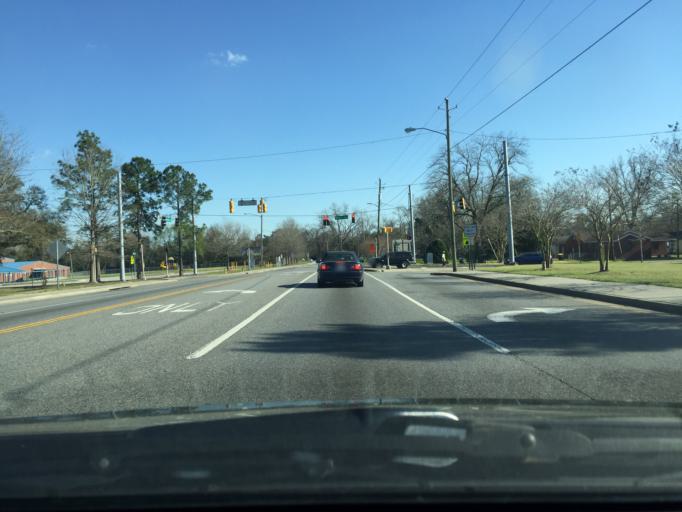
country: US
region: Georgia
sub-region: Chatham County
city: Savannah
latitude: 32.0651
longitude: -81.0793
